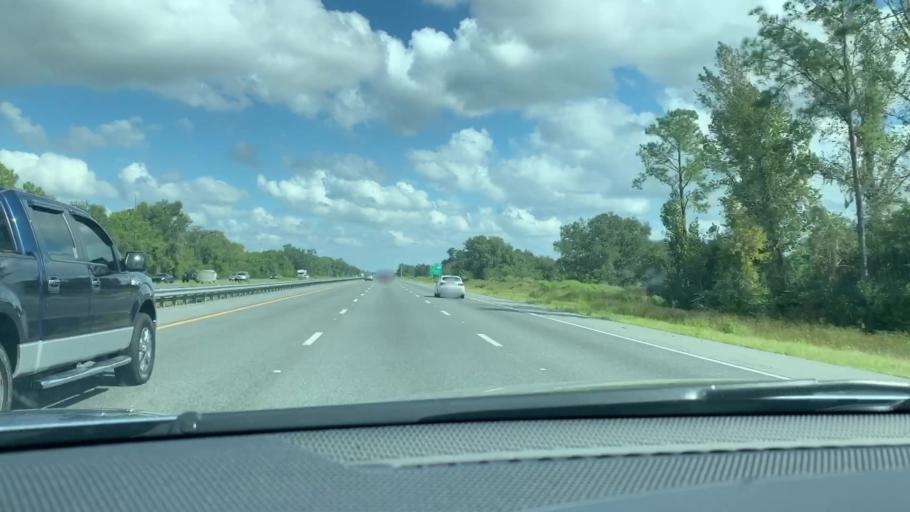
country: US
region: Florida
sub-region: Sumter County
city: Lake Panasoffkee
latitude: 28.7193
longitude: -82.1166
